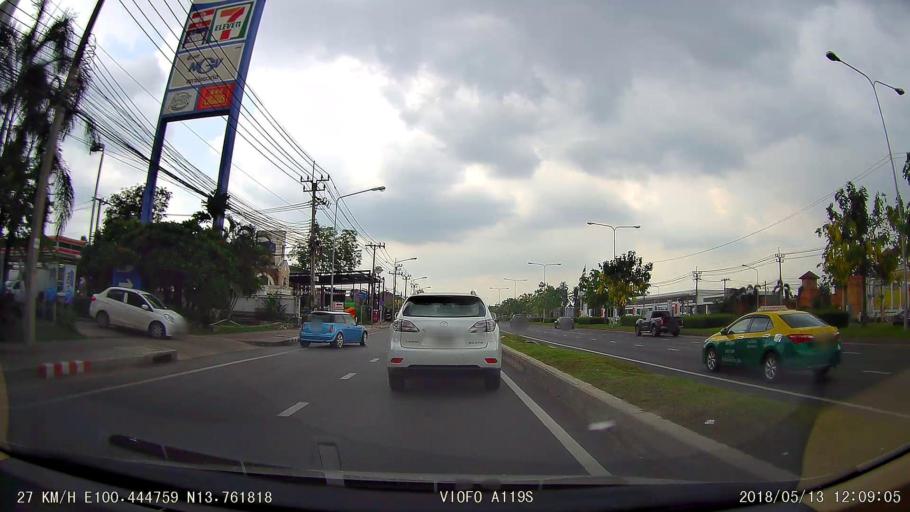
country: TH
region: Bangkok
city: Taling Chan
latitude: 13.7619
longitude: 100.4448
